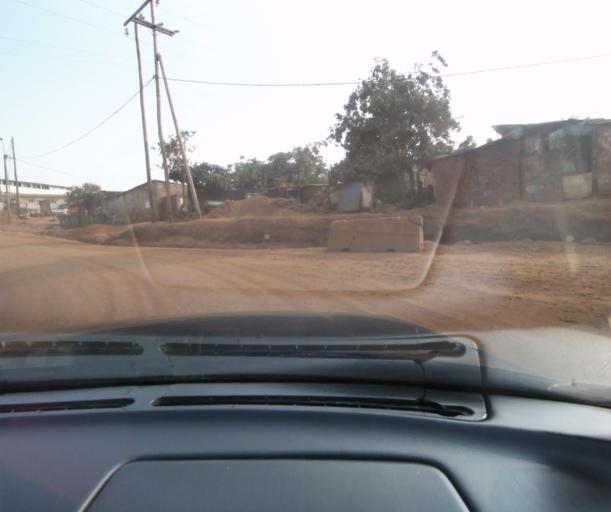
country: CM
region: Centre
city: Okoa
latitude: 3.9549
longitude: 11.5325
